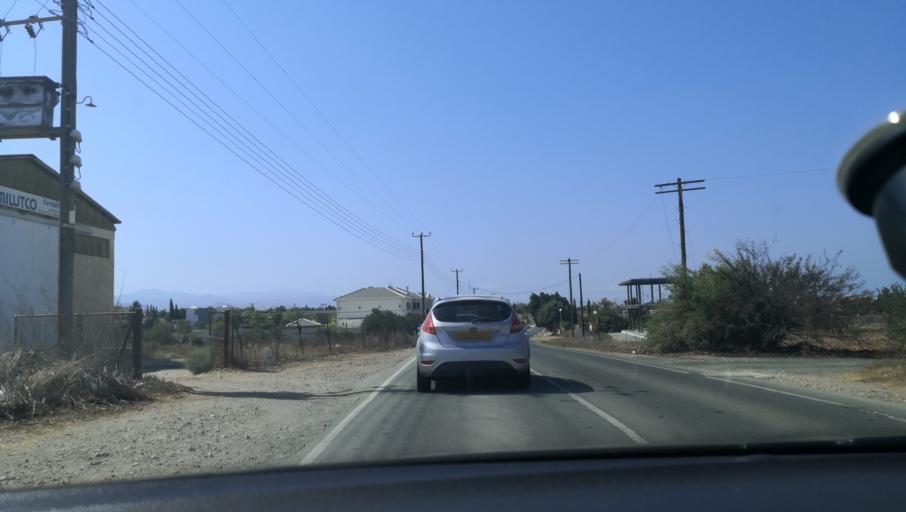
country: CY
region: Lefkosia
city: Pano Deftera
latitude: 35.1183
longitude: 33.2373
